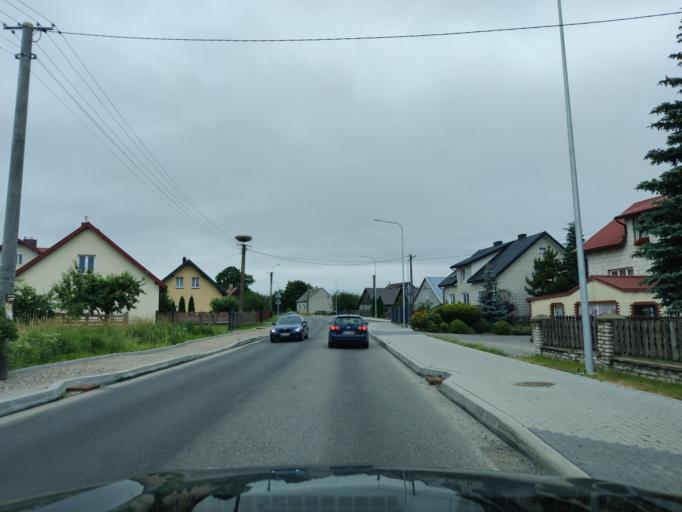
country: PL
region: Warmian-Masurian Voivodeship
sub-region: Powiat szczycienski
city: Rozogi
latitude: 53.4350
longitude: 21.3658
